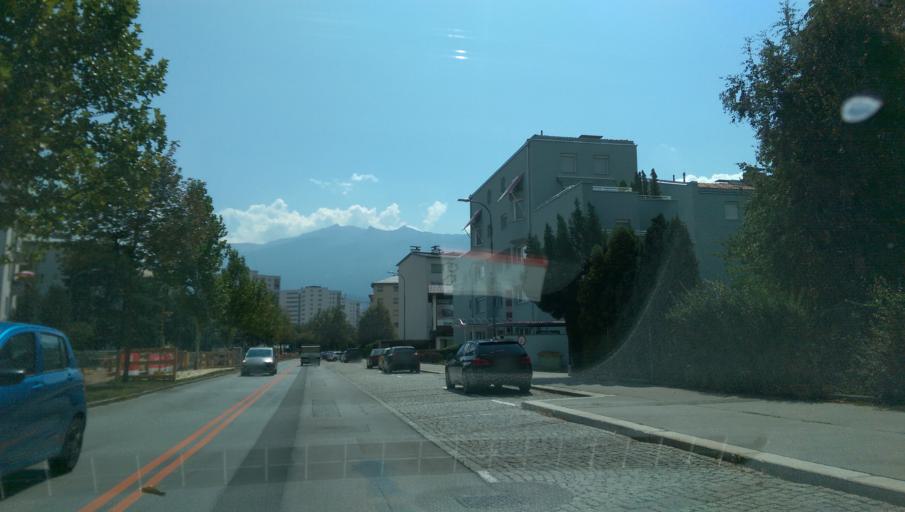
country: AT
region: Tyrol
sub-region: Innsbruck Stadt
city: Innsbruck
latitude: 47.2712
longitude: 11.4167
